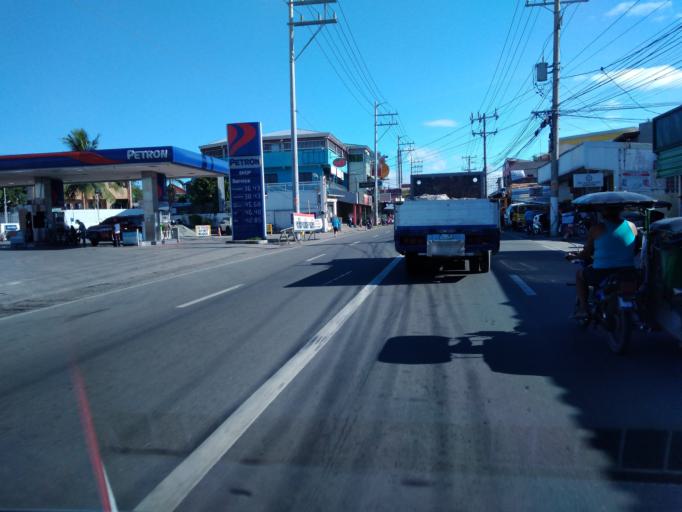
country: PH
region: Central Luzon
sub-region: Province of Bulacan
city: Santa Maria
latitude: 14.8220
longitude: 120.9529
